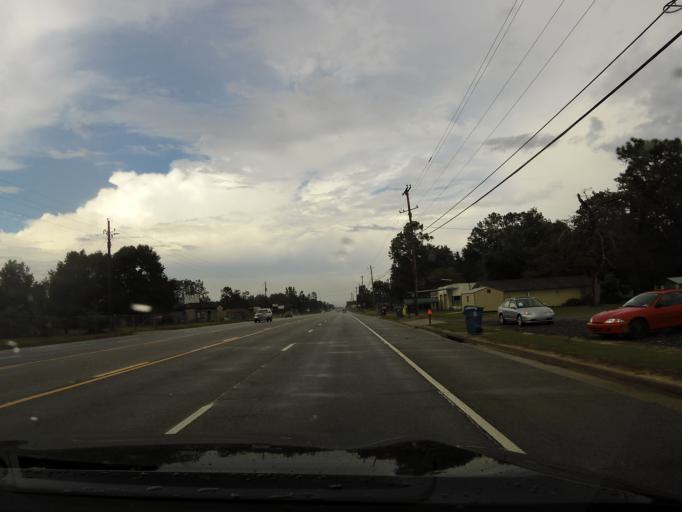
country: US
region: Georgia
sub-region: Wayne County
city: Jesup
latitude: 31.6311
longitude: -81.8642
